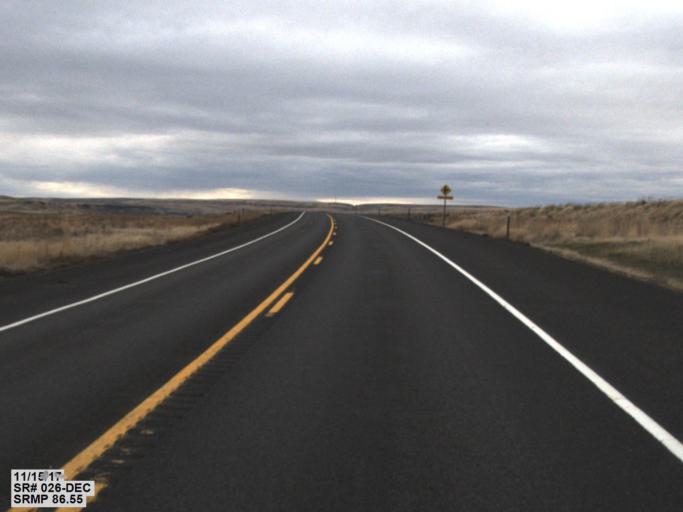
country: US
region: Washington
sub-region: Adams County
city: Ritzville
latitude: 46.7451
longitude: -118.2383
